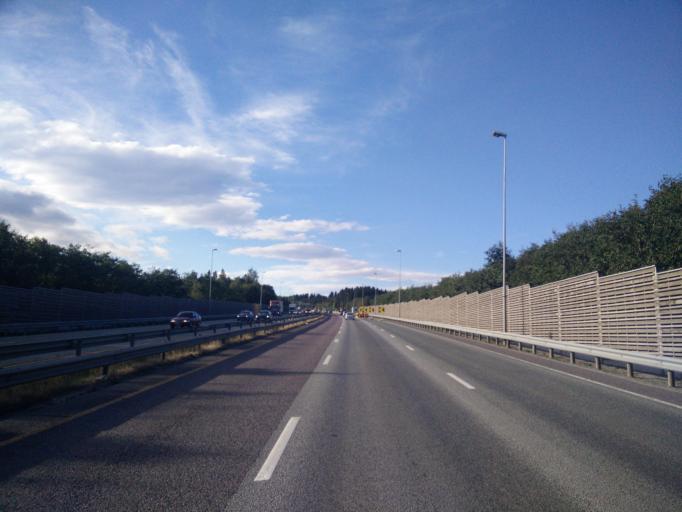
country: NO
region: Sor-Trondelag
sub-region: Trondheim
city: Trondheim
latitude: 63.3879
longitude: 10.3781
